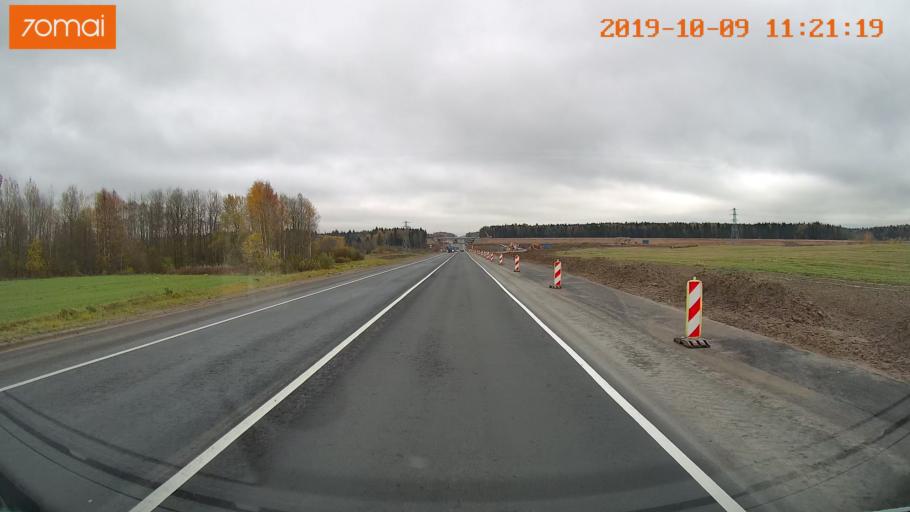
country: RU
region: Vologda
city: Vologda
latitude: 59.1405
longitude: 39.9484
